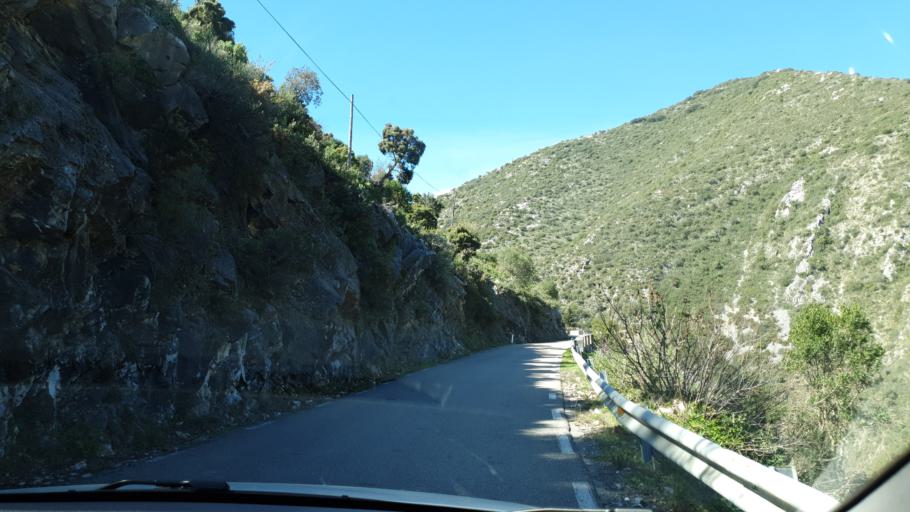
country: ES
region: Andalusia
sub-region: Provincia de Malaga
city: Ojen
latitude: 36.5893
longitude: -4.8775
